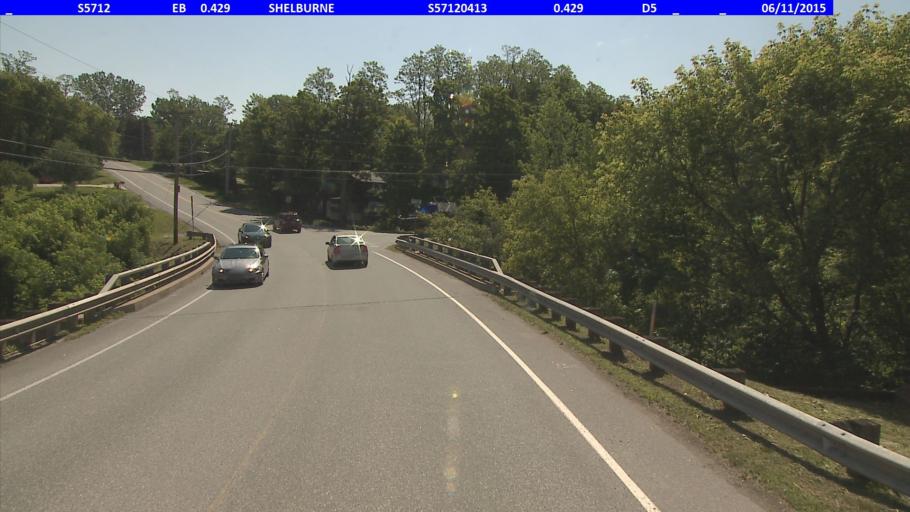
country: US
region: Vermont
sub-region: Chittenden County
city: Burlington
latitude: 44.3706
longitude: -73.2161
